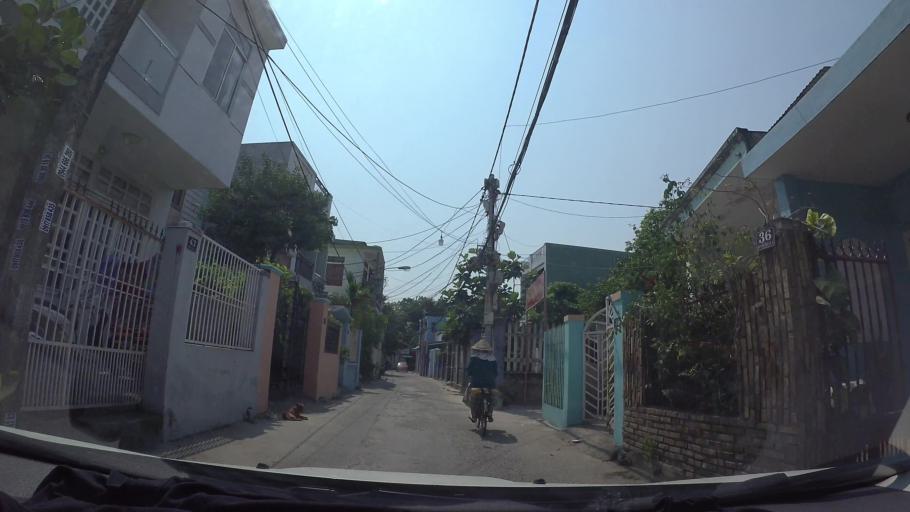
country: VN
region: Da Nang
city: Cam Le
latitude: 16.0128
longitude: 108.2023
